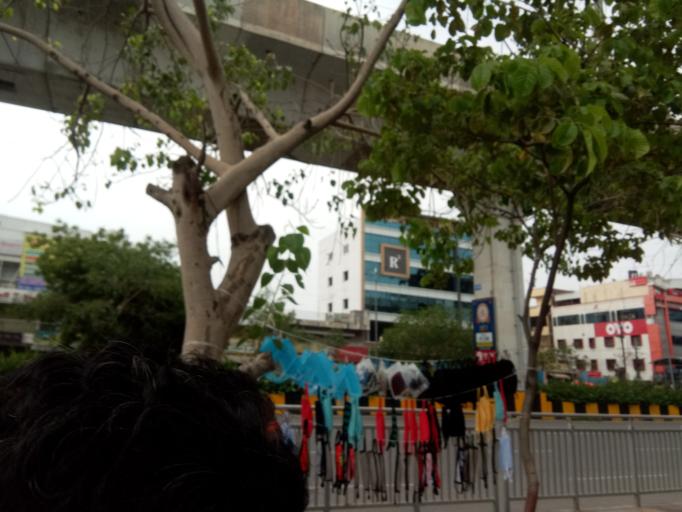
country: IN
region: Telangana
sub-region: Rangareddi
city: Lal Bahadur Nagar
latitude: 17.3505
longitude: 78.5472
